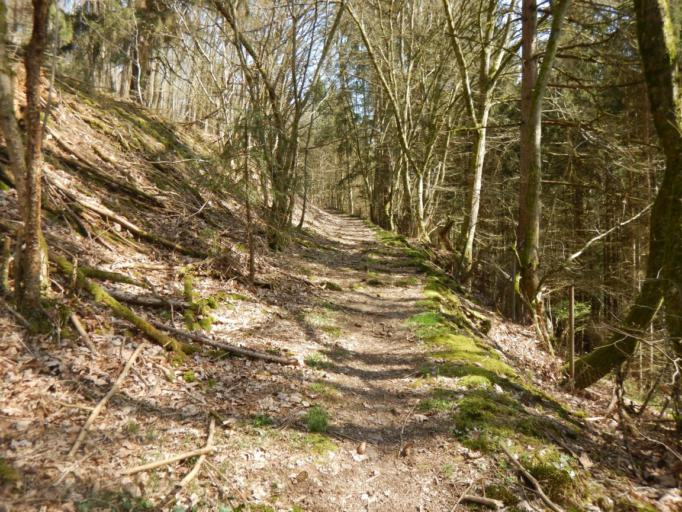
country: LU
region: Diekirch
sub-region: Canton de Diekirch
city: Bourscheid
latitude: 49.9347
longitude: 6.0693
